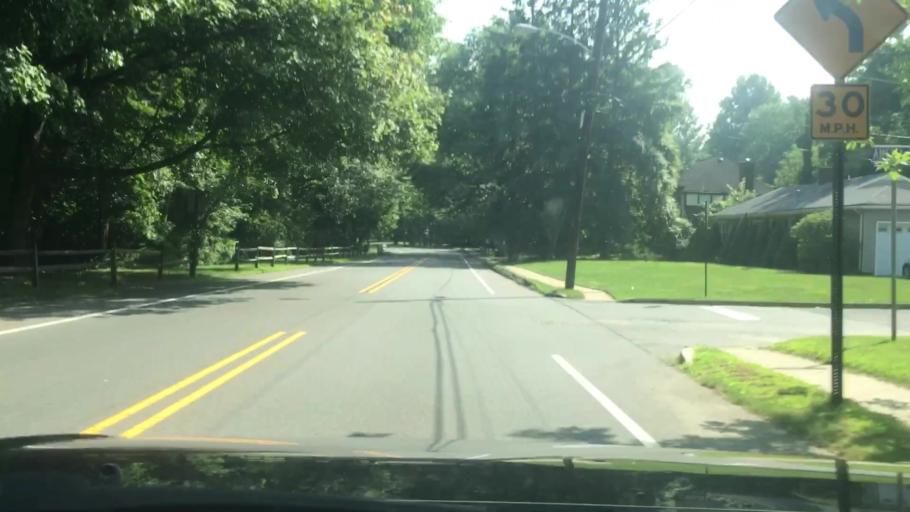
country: US
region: New Jersey
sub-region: Monmouth County
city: Little Silver
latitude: 40.3325
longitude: -74.0417
